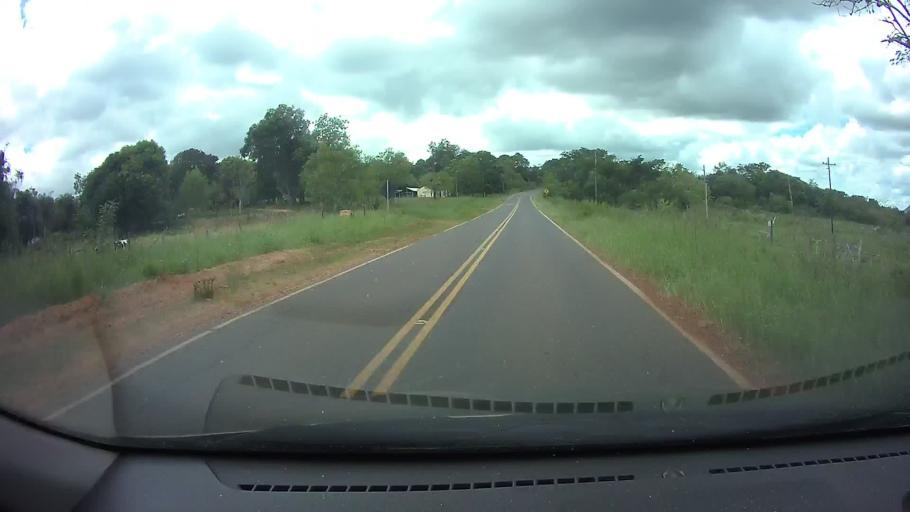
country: PY
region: Paraguari
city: Acahay
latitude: -25.9135
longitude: -57.0649
